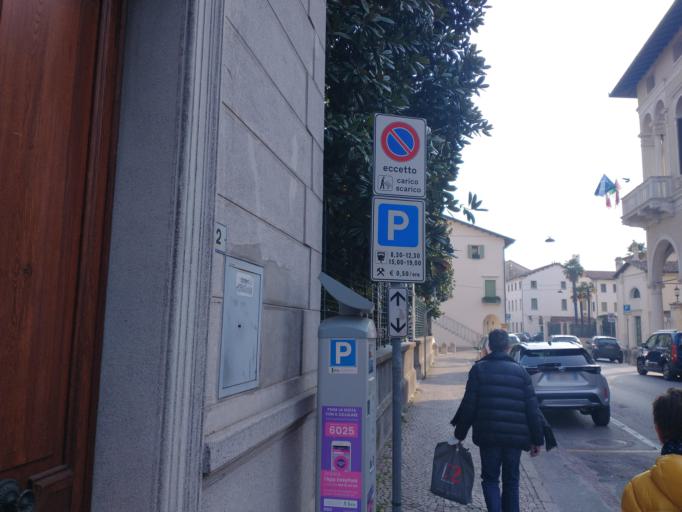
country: IT
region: Veneto
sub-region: Provincia di Venezia
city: Portogruaro
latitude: 45.7766
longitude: 12.8364
